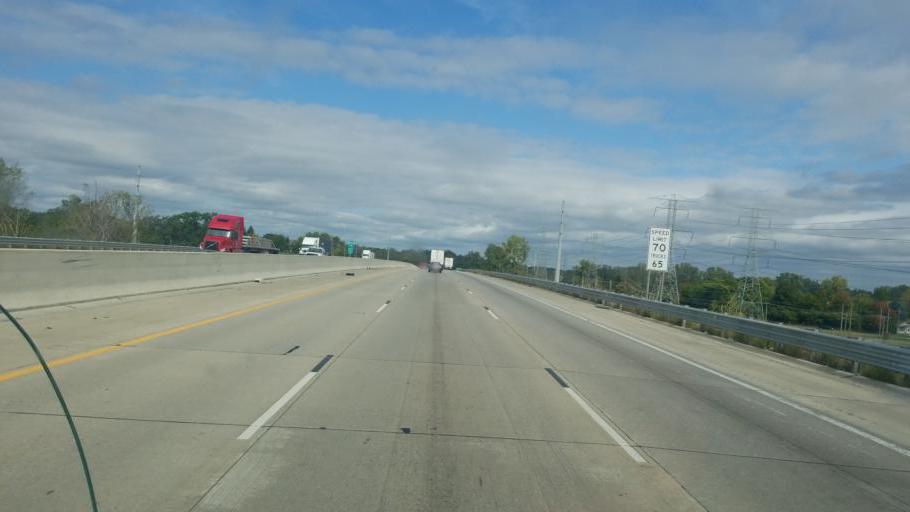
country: US
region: Michigan
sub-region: Monroe County
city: Detroit Beach
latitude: 41.9373
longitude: -83.3600
